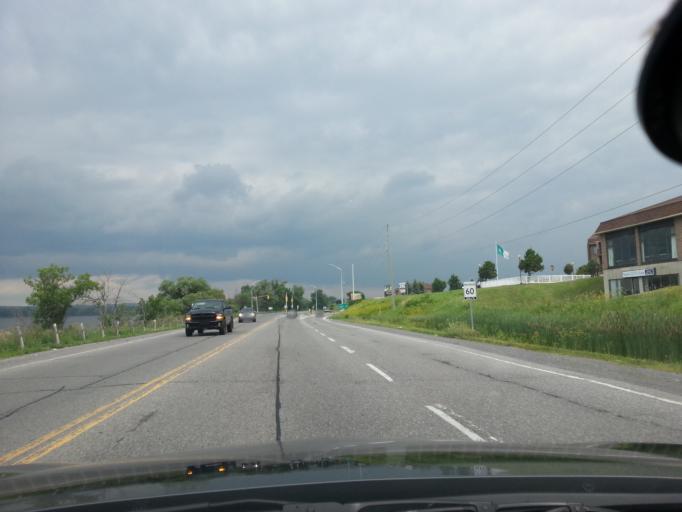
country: CA
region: Ontario
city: Clarence-Rockland
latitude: 45.5377
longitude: -75.3063
